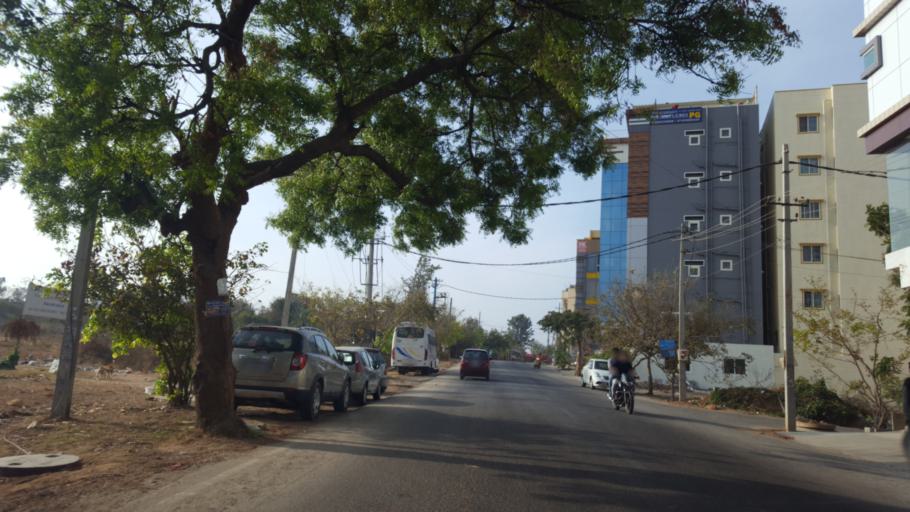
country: IN
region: Karnataka
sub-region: Bangalore Urban
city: Bangalore
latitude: 12.9139
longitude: 77.5006
